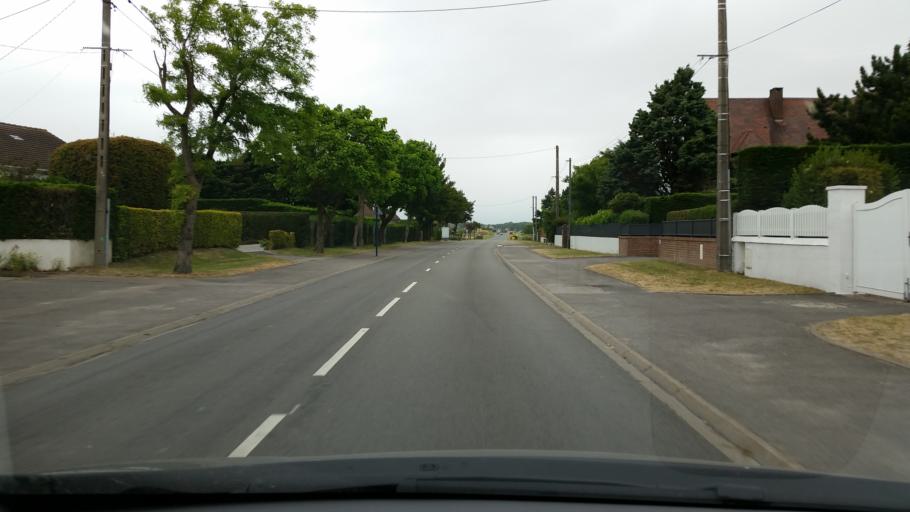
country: FR
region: Nord-Pas-de-Calais
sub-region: Departement du Pas-de-Calais
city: Marck
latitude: 50.9526
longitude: 1.9397
